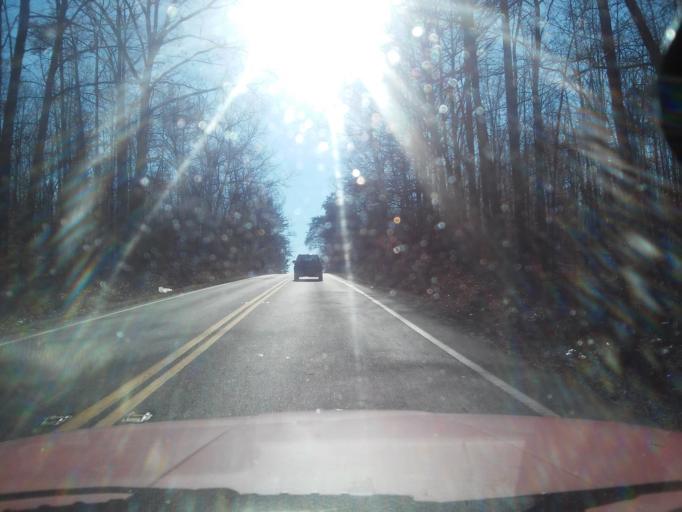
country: US
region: Virginia
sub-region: Orange County
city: Gordonsville
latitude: 37.9985
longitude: -78.1950
